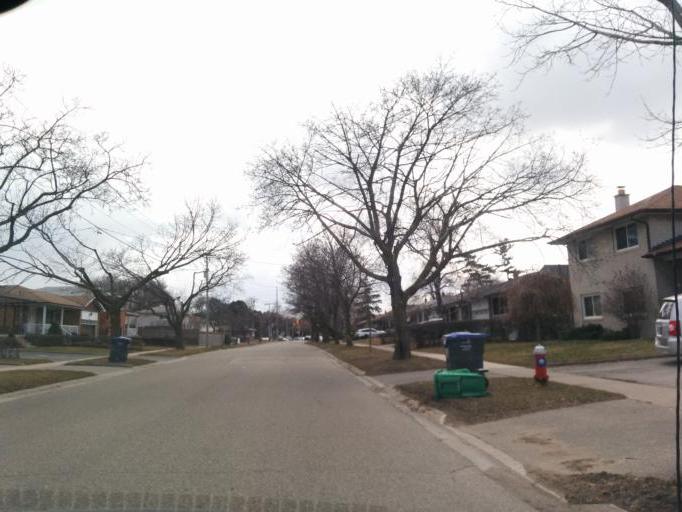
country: CA
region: Ontario
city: Etobicoke
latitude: 43.6012
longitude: -79.5688
